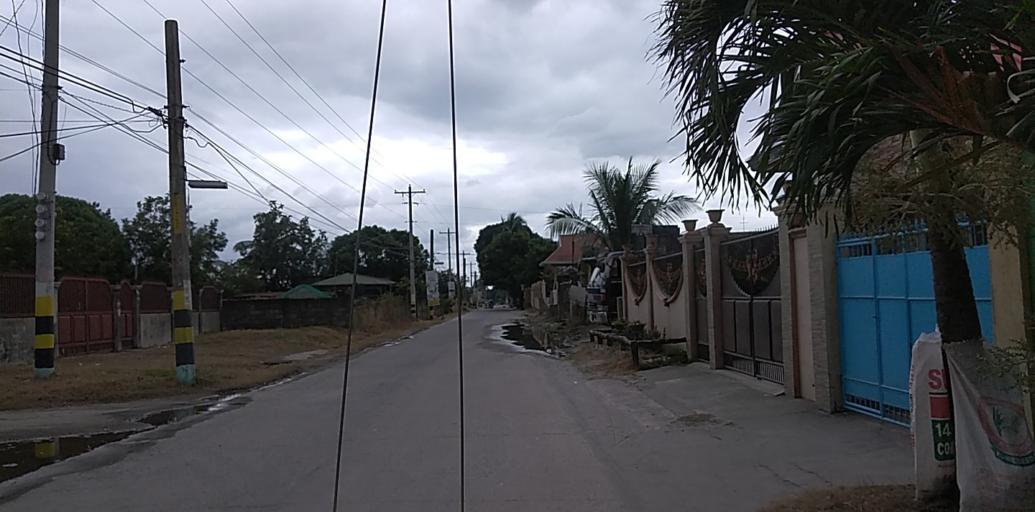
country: PH
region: Central Luzon
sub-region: Province of Pampanga
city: Pio
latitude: 15.0472
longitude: 120.5316
